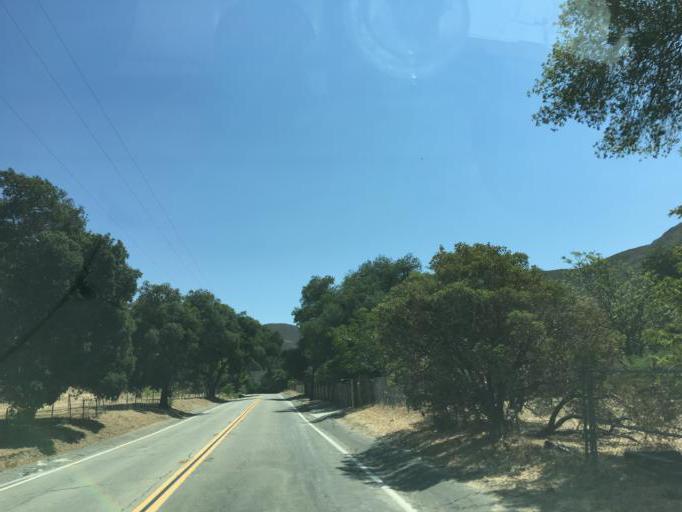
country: US
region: California
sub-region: Los Angeles County
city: Green Valley
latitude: 34.6288
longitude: -118.4031
